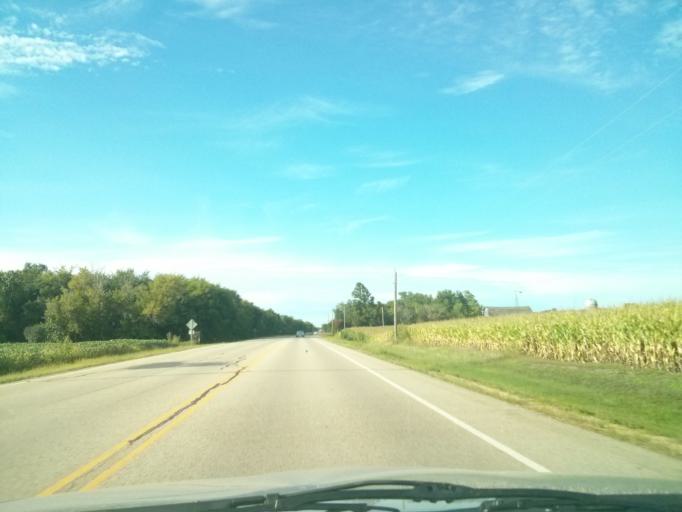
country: US
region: Minnesota
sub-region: Washington County
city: Lake Saint Croix Beach
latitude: 44.9322
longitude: -92.7317
